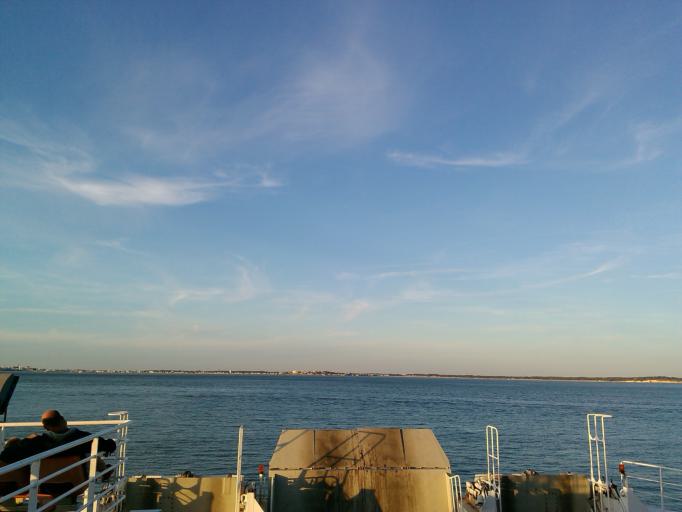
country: FR
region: Poitou-Charentes
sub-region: Departement de la Charente-Maritime
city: Saint-Georges-de-Didonne
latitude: 45.5685
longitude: -1.0618
